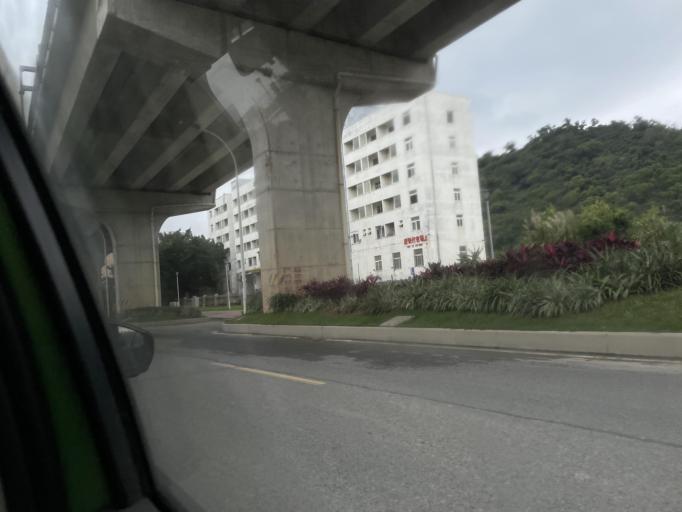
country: CN
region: Guangdong
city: Nanping
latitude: 22.1765
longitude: 113.4812
